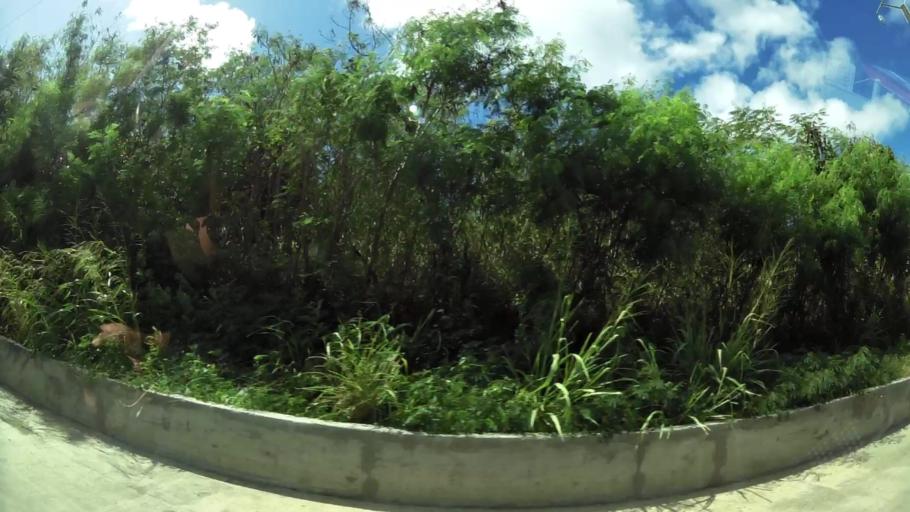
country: GP
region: Guadeloupe
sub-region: Guadeloupe
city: Petit-Canal
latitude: 16.4149
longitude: -61.4709
